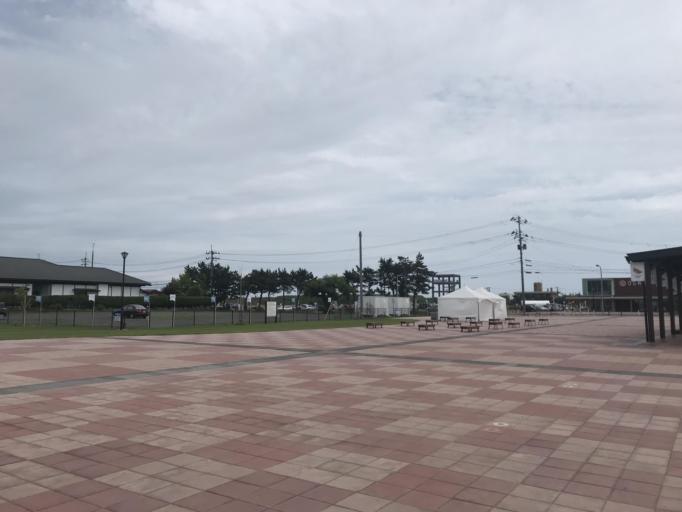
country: JP
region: Akita
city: Tenno
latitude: 39.8835
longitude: 139.8479
